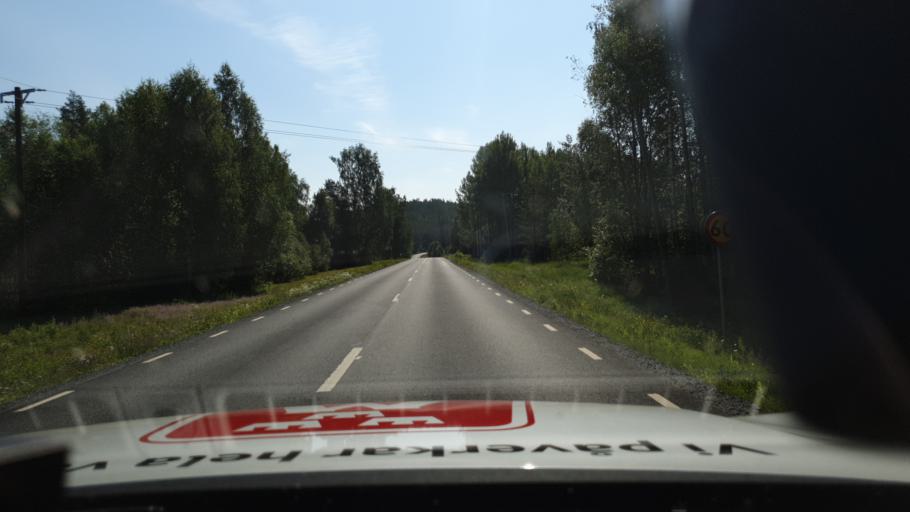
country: SE
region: Norrbotten
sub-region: Bodens Kommun
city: Saevast
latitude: 65.8325
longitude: 21.8713
